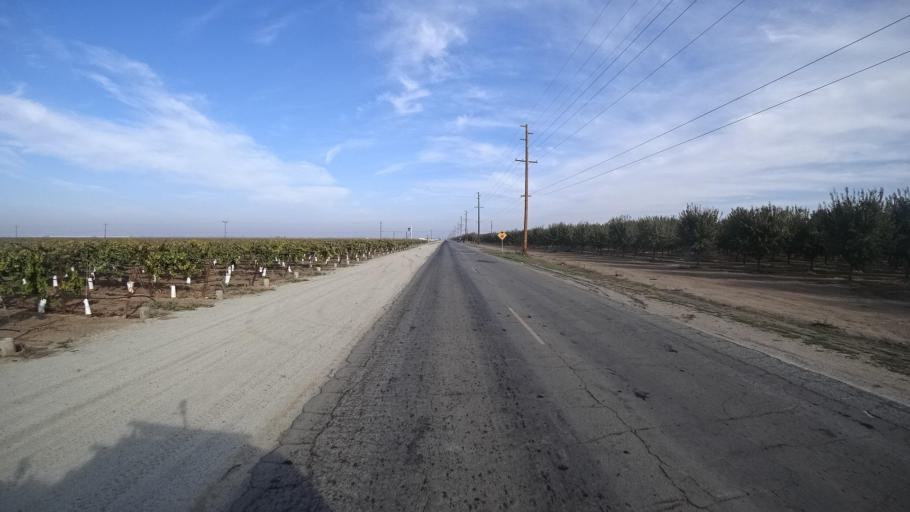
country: US
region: California
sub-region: Kern County
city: McFarland
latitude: 35.7161
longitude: -119.2051
